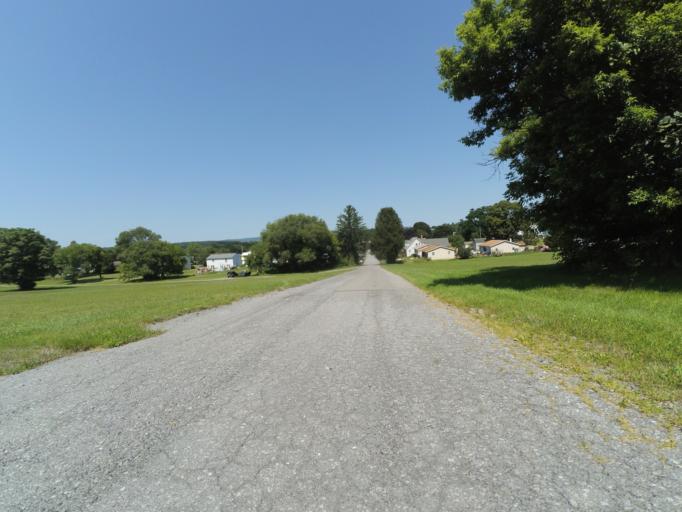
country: US
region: Pennsylvania
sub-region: Centre County
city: Pleasant Gap
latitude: 40.8650
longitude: -77.7462
